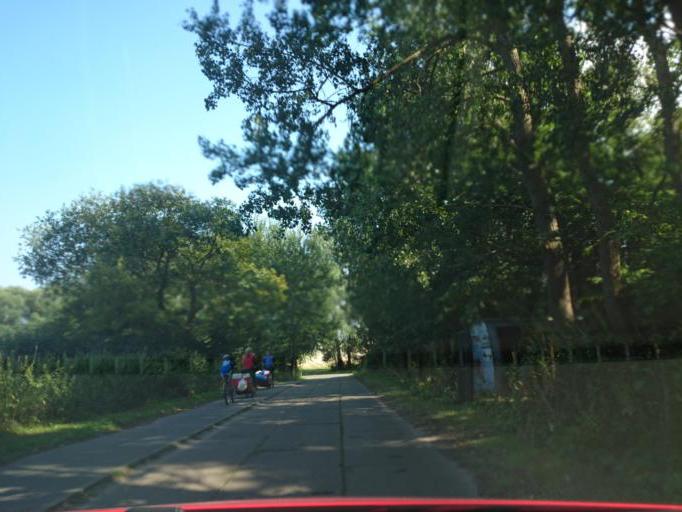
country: DE
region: Mecklenburg-Vorpommern
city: Barth
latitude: 54.3673
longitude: 12.7533
